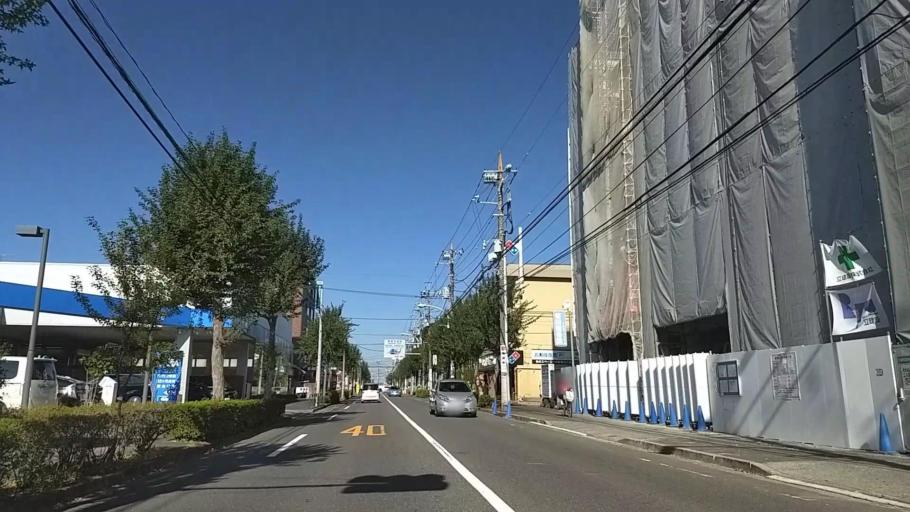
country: JP
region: Tokyo
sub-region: Machida-shi
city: Machida
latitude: 35.5550
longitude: 139.4417
